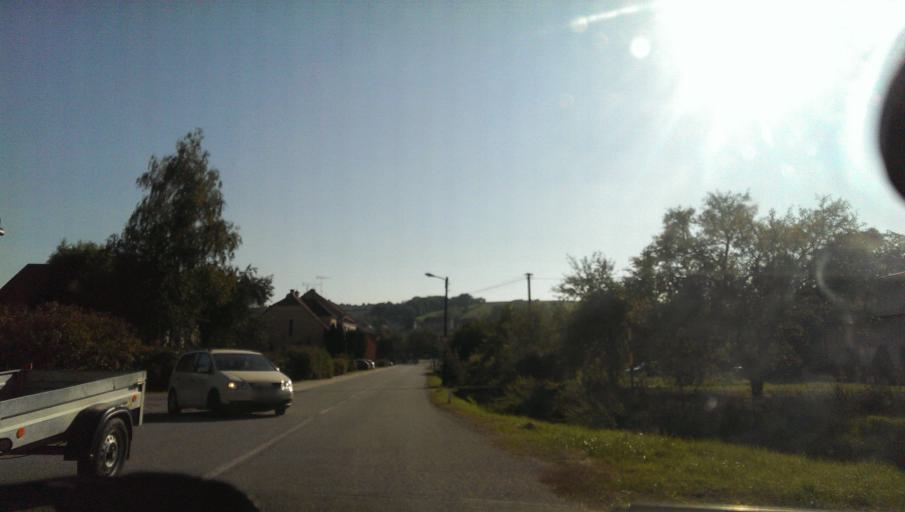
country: CZ
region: Zlin
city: Popovice
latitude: 49.0459
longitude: 17.5281
